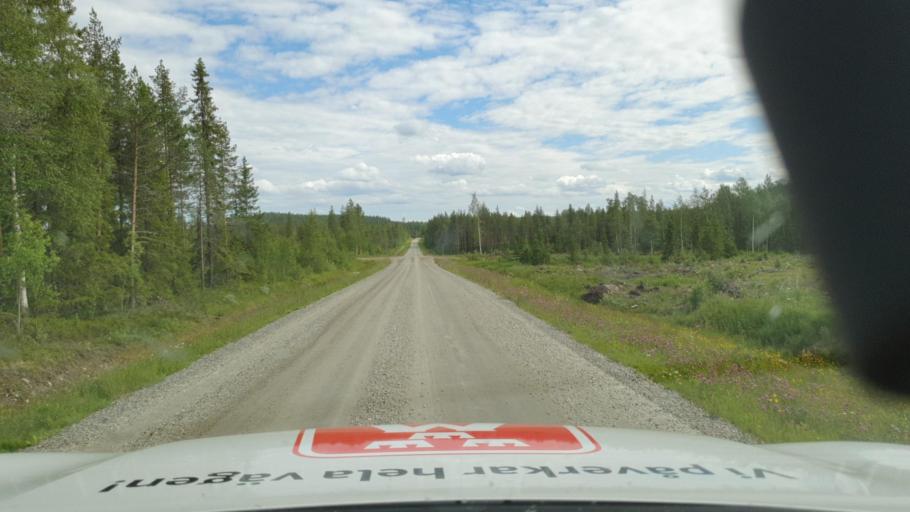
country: SE
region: Vaesterbotten
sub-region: Norsjo Kommun
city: Norsjoe
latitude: 64.8530
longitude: 19.5068
